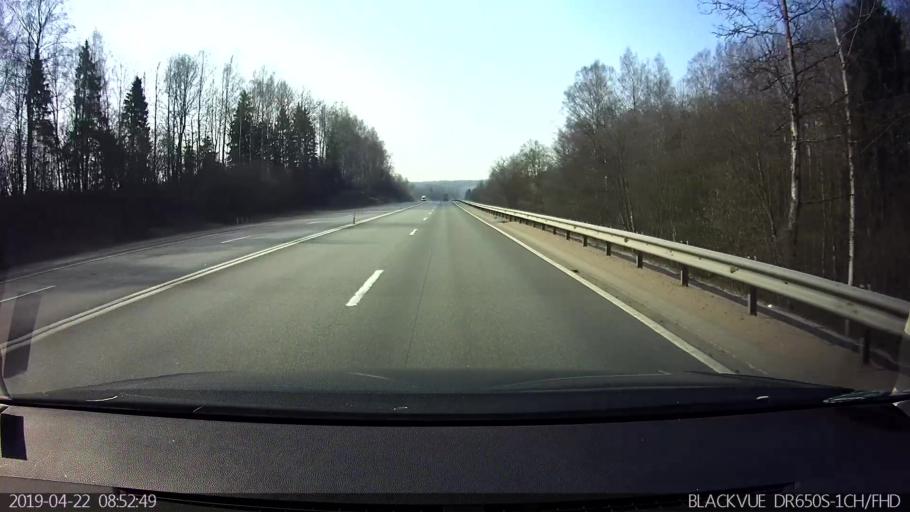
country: RU
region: Smolensk
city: Pechersk
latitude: 54.9035
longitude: 32.1215
